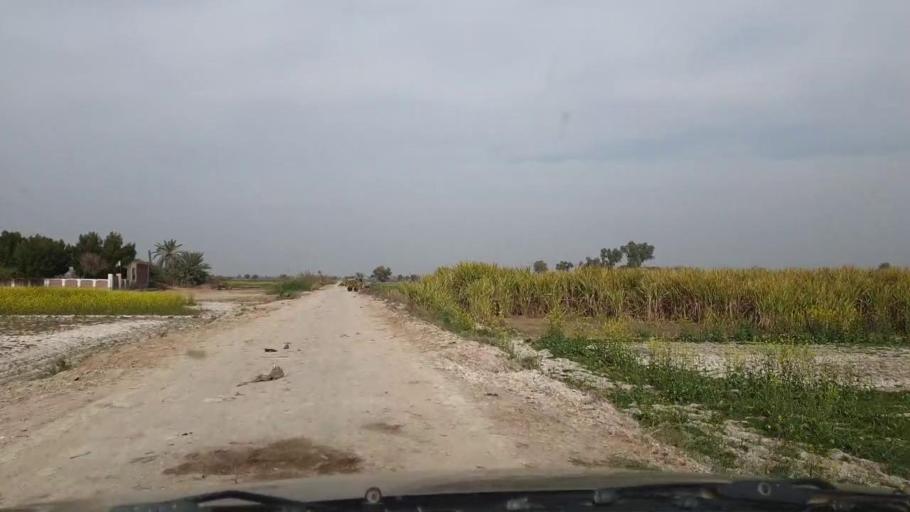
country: PK
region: Sindh
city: Sinjhoro
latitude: 26.0914
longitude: 68.8278
